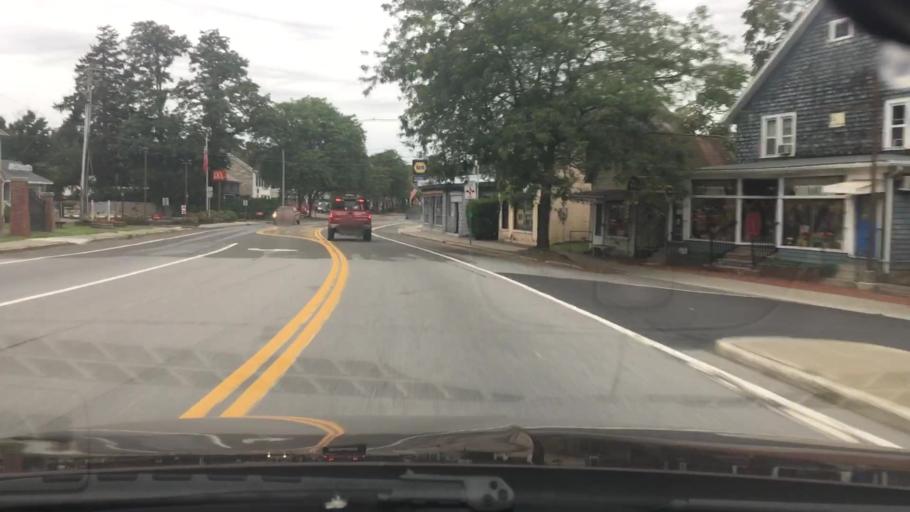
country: US
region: New York
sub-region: Dutchess County
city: Pleasant Valley
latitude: 41.7451
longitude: -73.8219
